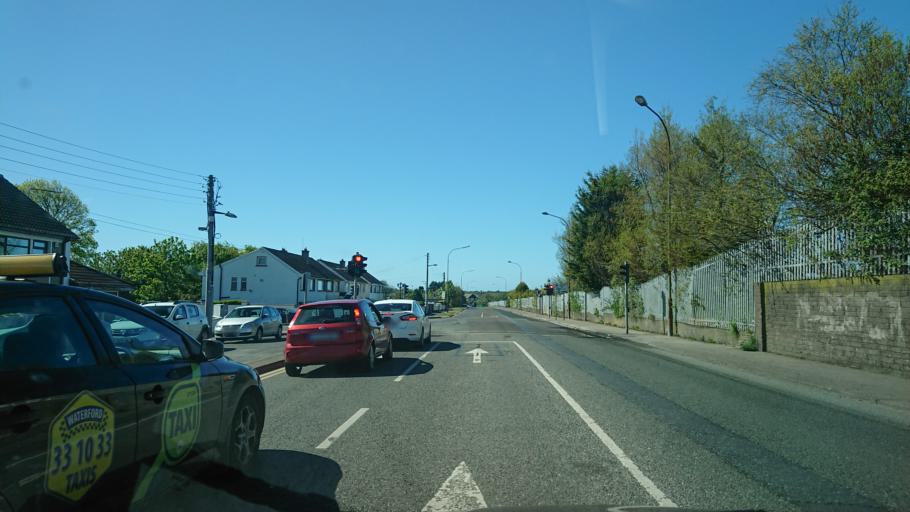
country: IE
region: Munster
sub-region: Waterford
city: Waterford
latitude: 52.2488
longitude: -7.1276
